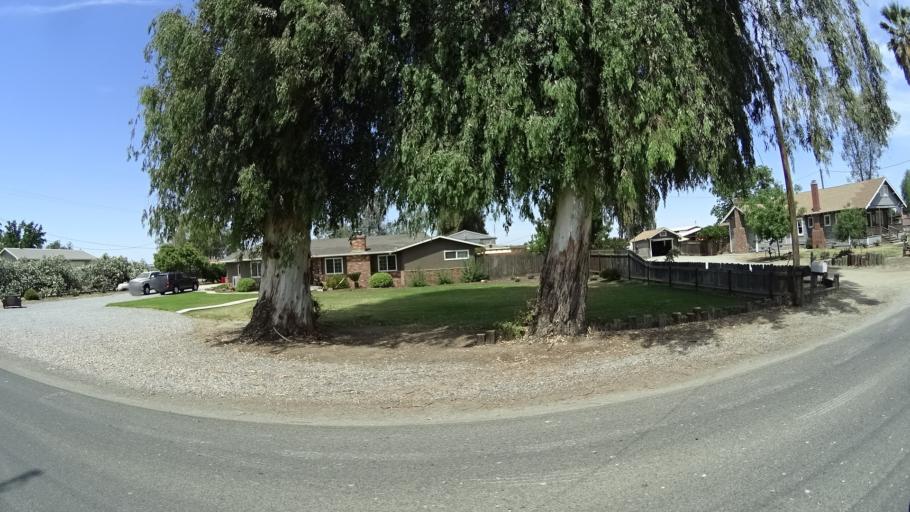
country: US
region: California
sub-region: Kings County
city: Armona
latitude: 36.3502
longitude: -119.6910
